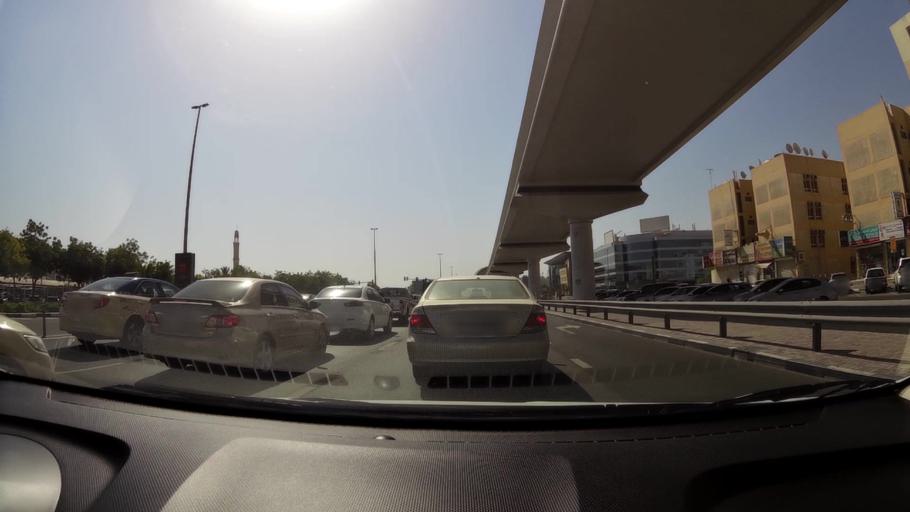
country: AE
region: Ash Shariqah
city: Sharjah
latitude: 25.2712
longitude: 55.3726
